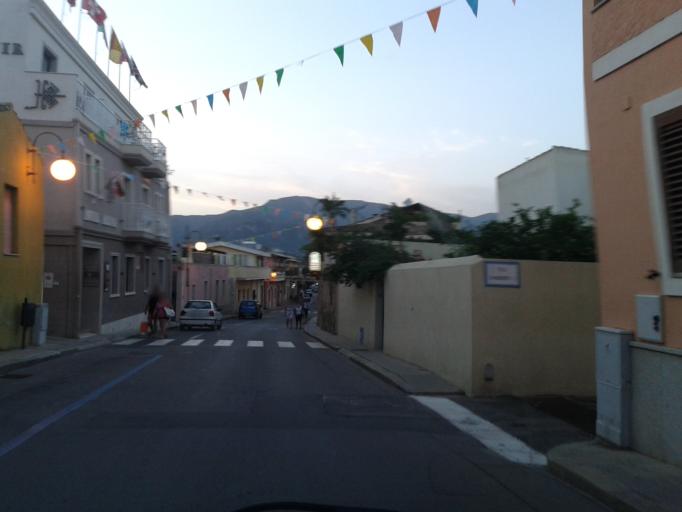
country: IT
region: Sardinia
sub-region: Provincia di Cagliari
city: Villasimius
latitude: 39.1448
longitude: 9.5179
